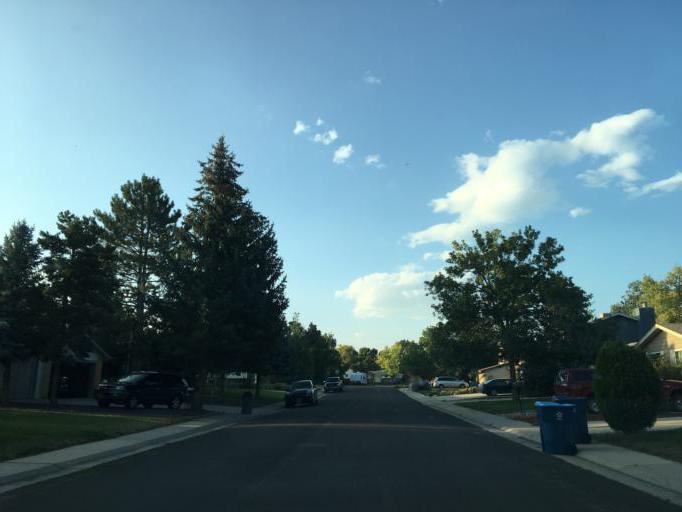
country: US
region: Colorado
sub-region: Jefferson County
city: Applewood
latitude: 39.7897
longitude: -105.1497
